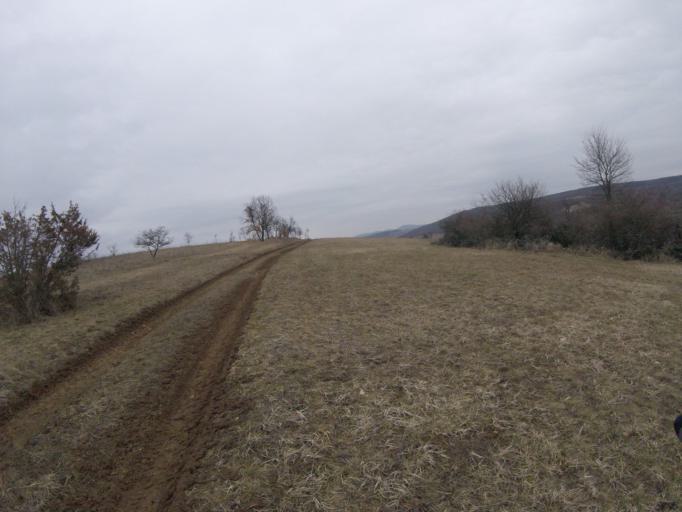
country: HU
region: Borsod-Abauj-Zemplen
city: Rudabanya
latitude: 48.4669
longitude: 20.6069
